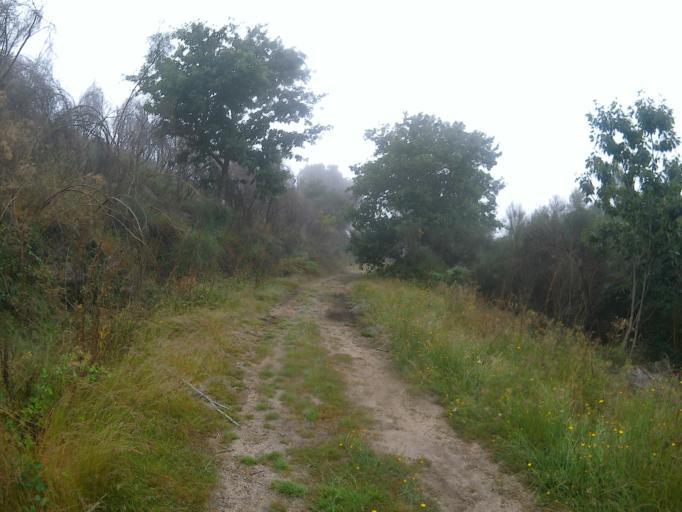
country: PT
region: Viana do Castelo
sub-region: Ponte de Lima
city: Ponte de Lima
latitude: 41.6978
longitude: -8.6073
